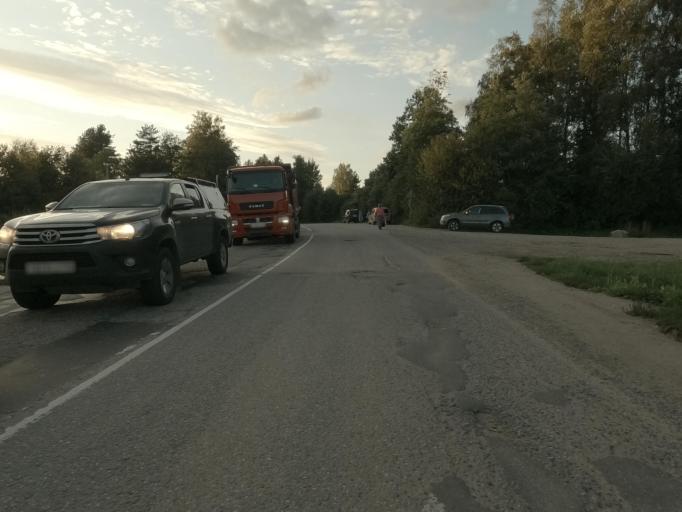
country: RU
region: Leningrad
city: Mga
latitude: 59.7638
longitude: 30.9851
